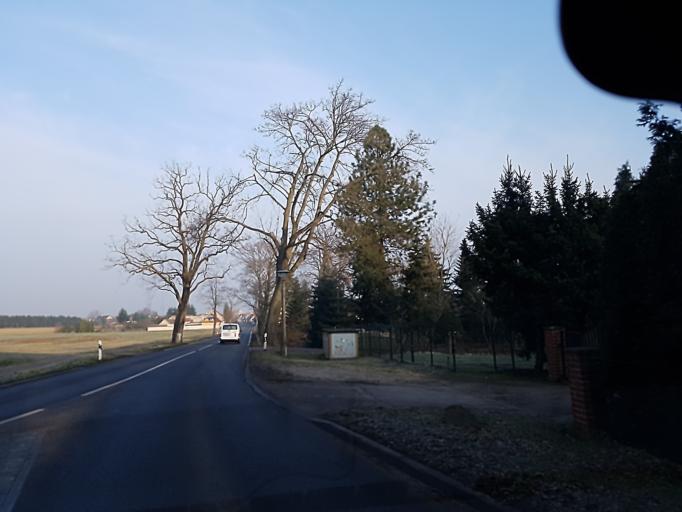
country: DE
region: Brandenburg
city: Gorzke
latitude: 52.1651
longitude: 12.3811
